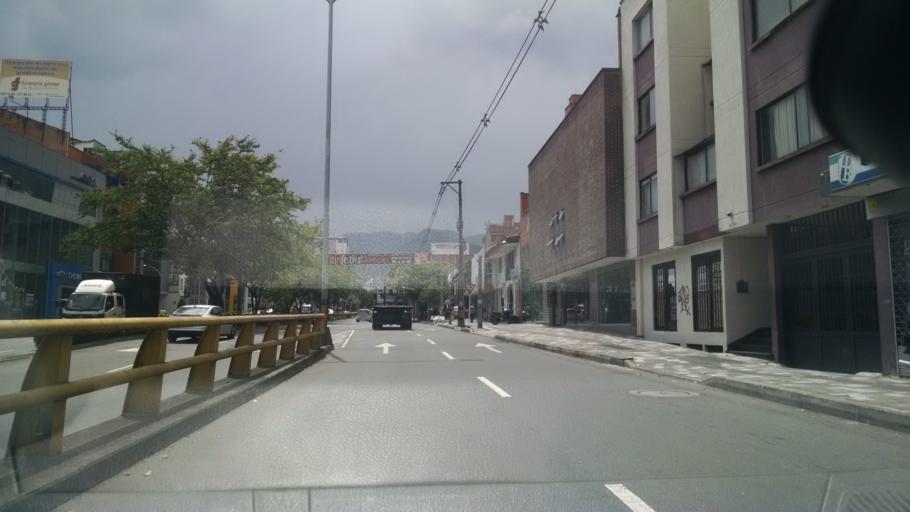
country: CO
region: Antioquia
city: Medellin
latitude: 6.2393
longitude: -75.5911
